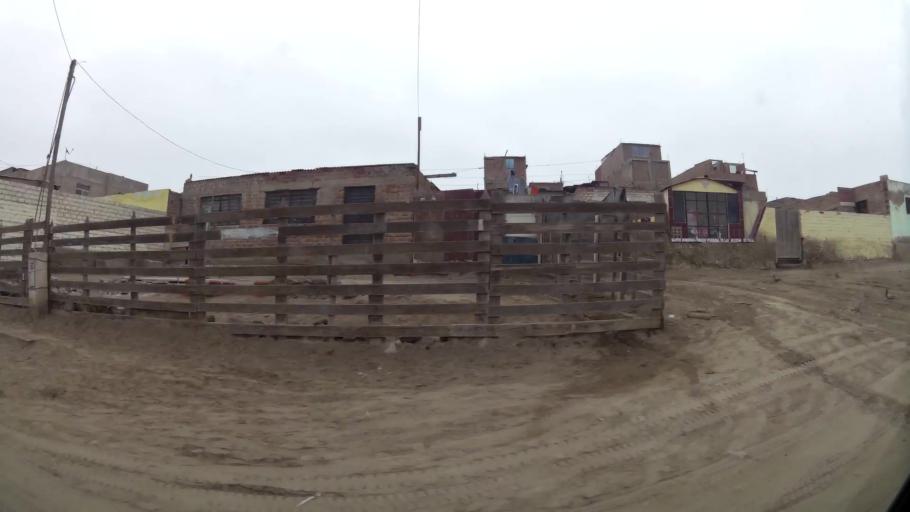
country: PE
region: Lima
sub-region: Lima
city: Surco
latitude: -12.2056
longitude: -76.9881
